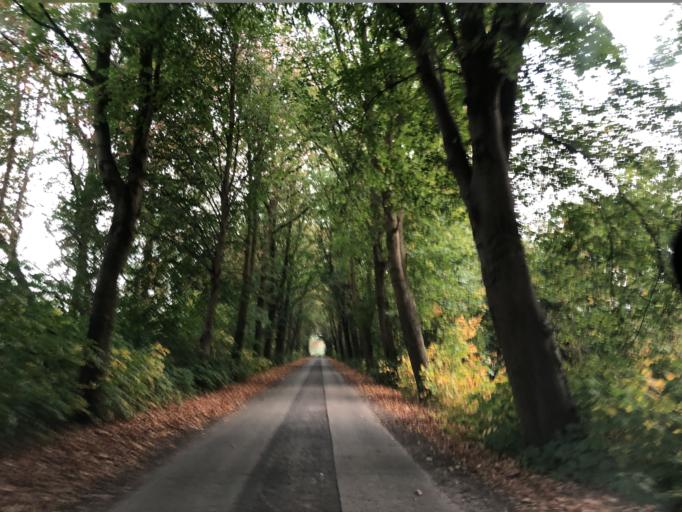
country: DE
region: Lower Saxony
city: Papenburg
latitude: 53.0498
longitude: 7.4281
